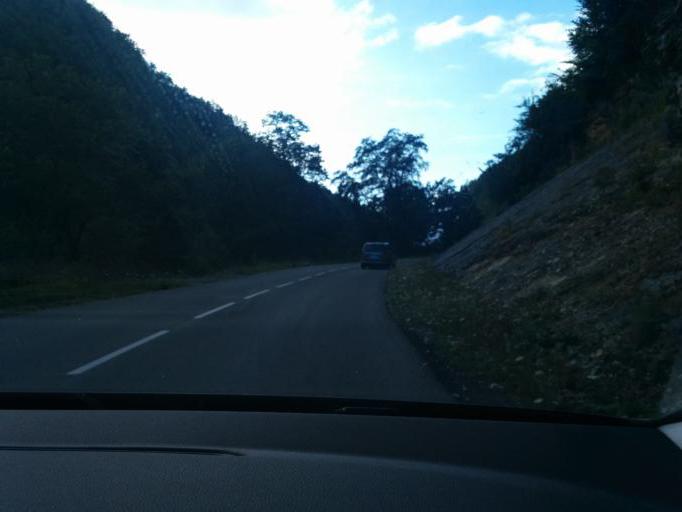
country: FR
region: Franche-Comte
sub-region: Departement du Jura
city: Saint-Lupicin
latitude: 46.4406
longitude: 5.8105
